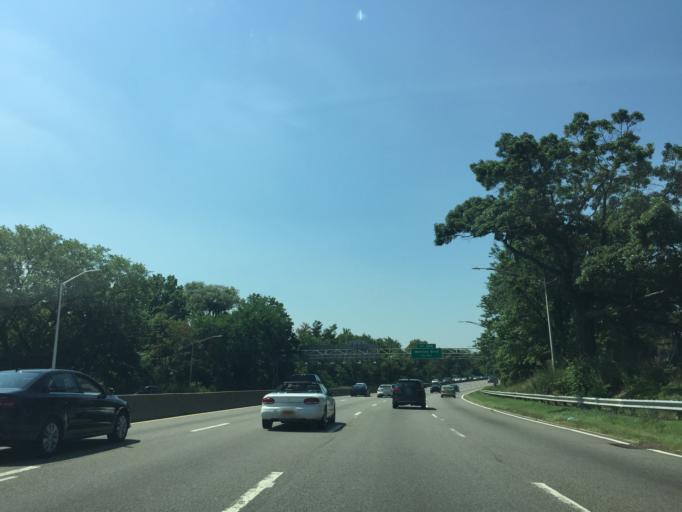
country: US
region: New York
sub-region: Nassau County
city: Elmont
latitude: 40.6846
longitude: -73.7264
